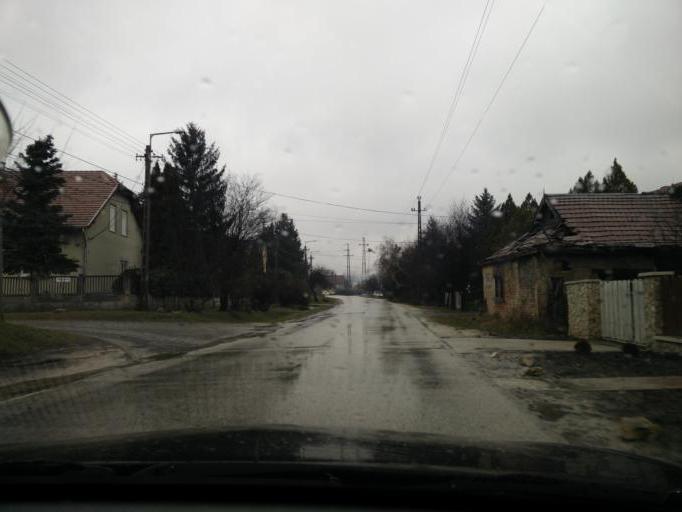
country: HU
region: Pest
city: Pilisszentivan
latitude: 47.6126
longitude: 18.9030
